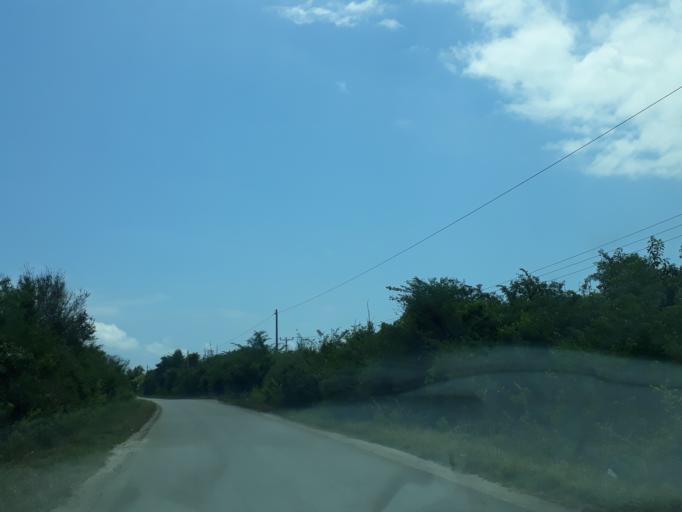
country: TZ
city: Kiwengwa
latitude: -5.9922
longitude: 39.3666
